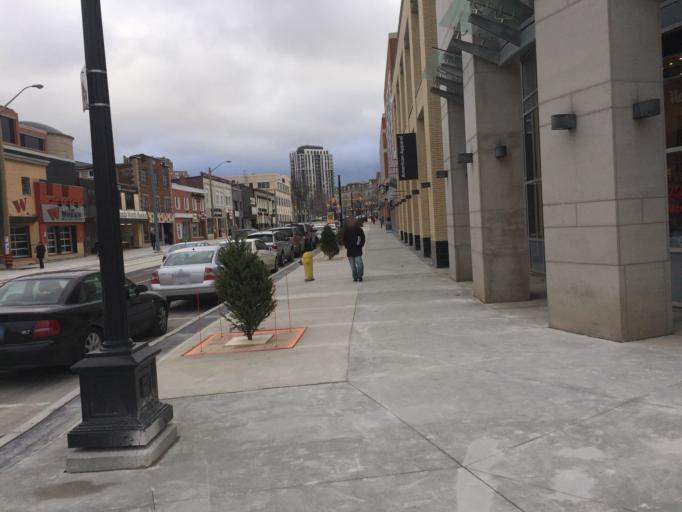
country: CA
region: Ontario
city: Waterloo
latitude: 43.4635
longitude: -80.5221
